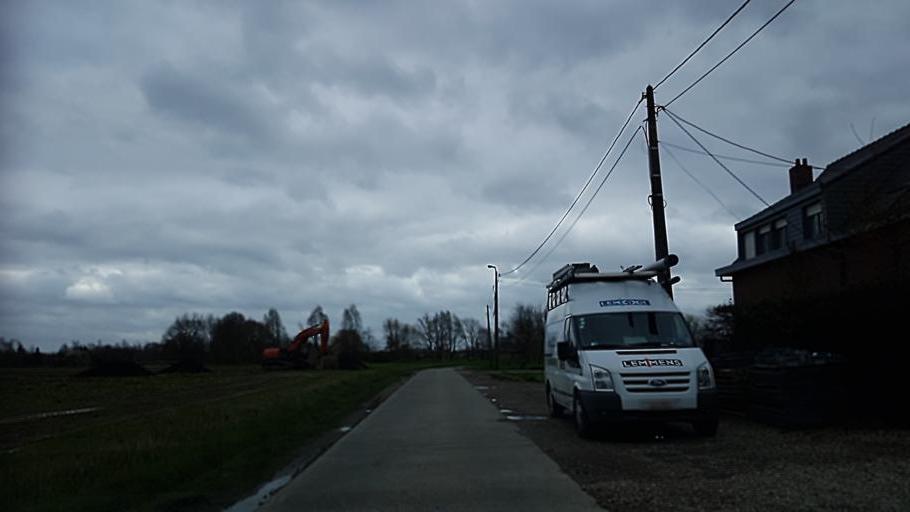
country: BE
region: Flanders
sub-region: Provincie Antwerpen
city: Lint
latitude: 51.1116
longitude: 4.5030
